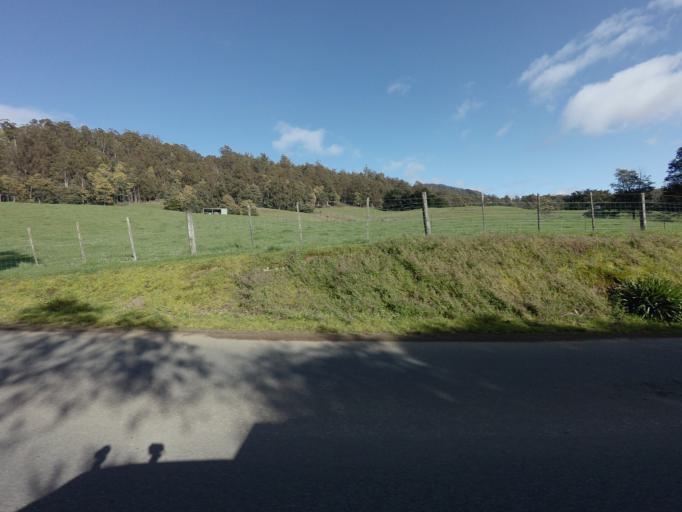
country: AU
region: Tasmania
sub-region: Huon Valley
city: Geeveston
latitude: -43.2437
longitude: 146.9912
